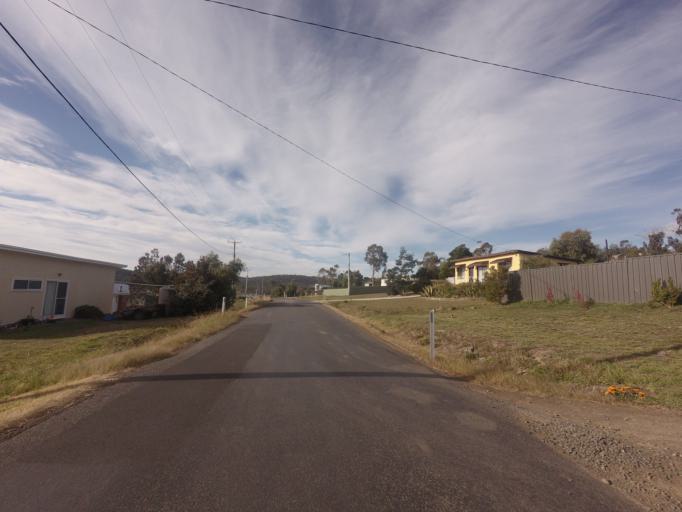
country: AU
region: Tasmania
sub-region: Sorell
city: Sorell
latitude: -42.9481
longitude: 147.8523
